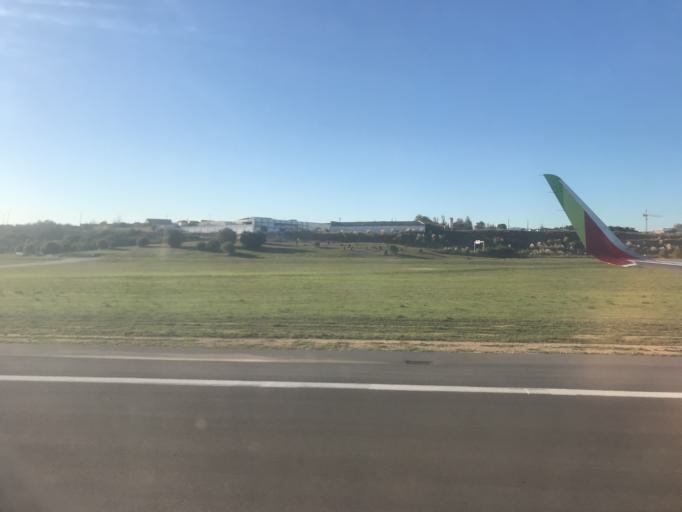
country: PT
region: Lisbon
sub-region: Loures
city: Camarate
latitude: 38.7805
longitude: -9.1364
